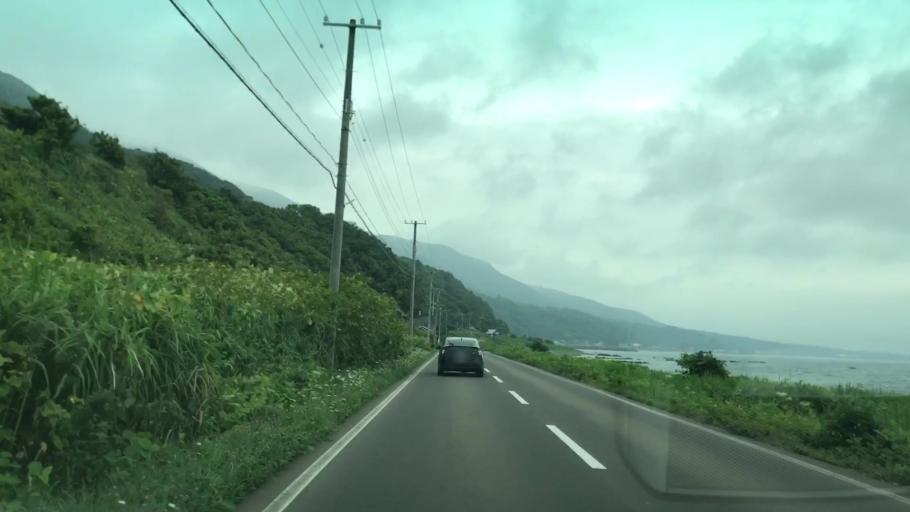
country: JP
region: Hokkaido
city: Iwanai
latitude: 42.8063
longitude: 140.3055
